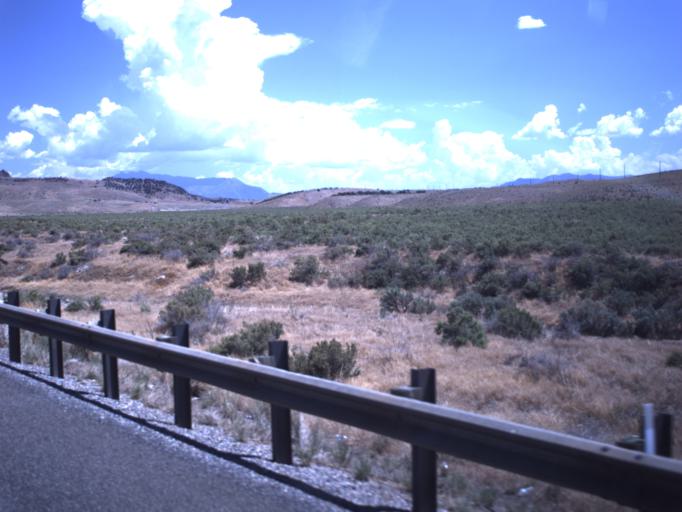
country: US
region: Utah
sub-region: Juab County
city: Nephi
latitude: 39.6262
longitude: -112.1219
